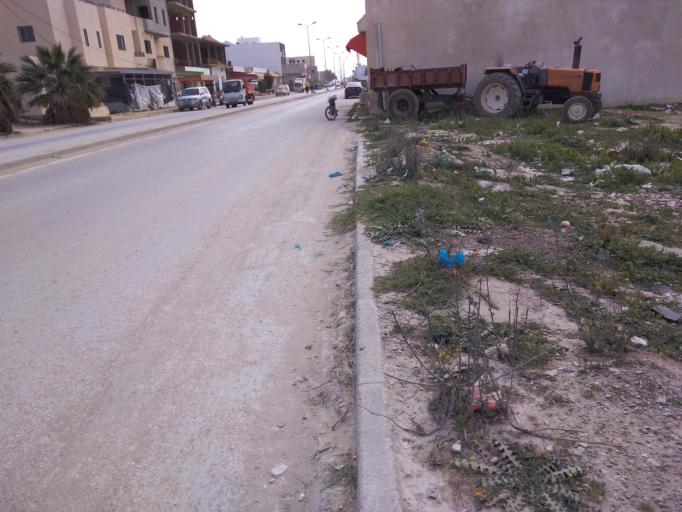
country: TN
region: Ariana
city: Ariana
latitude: 36.9475
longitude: 10.1737
